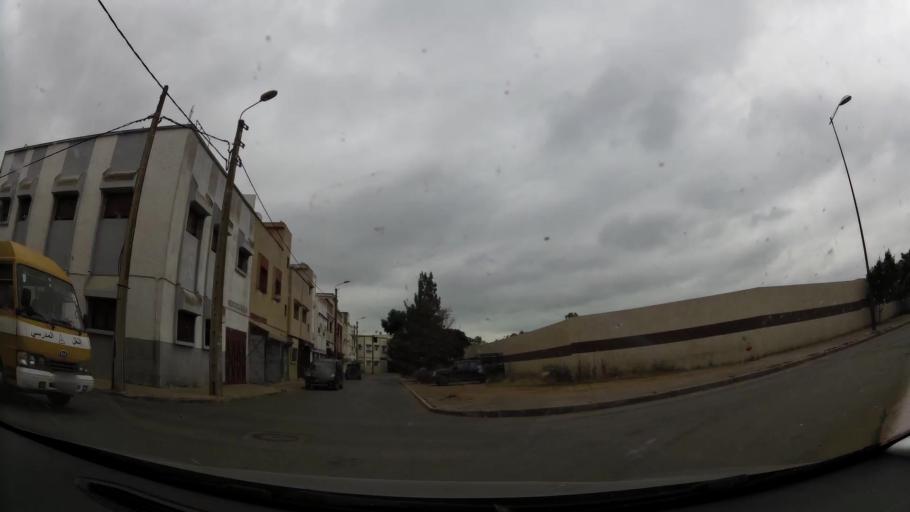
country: MA
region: Rabat-Sale-Zemmour-Zaer
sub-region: Rabat
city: Rabat
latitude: 33.9755
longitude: -6.8139
